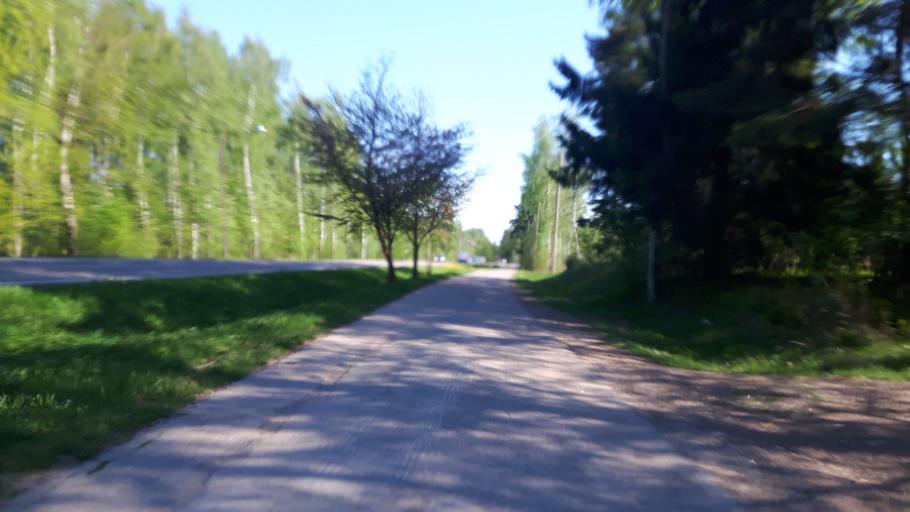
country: FI
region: Kymenlaakso
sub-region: Kotka-Hamina
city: Kotka
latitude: 60.4594
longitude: 26.8868
